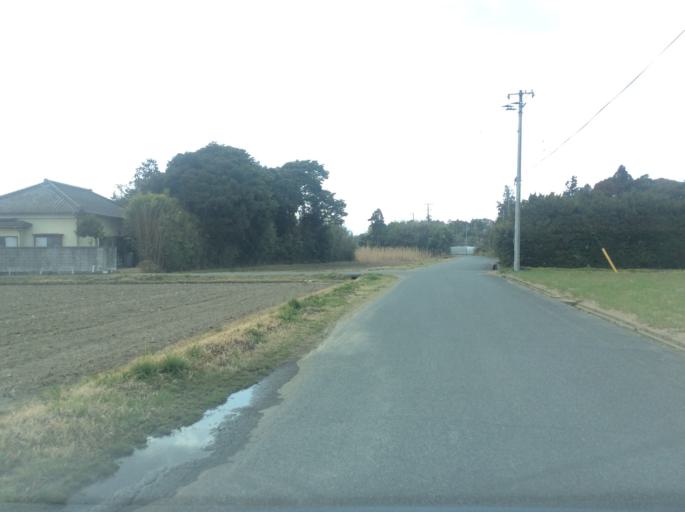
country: JP
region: Fukushima
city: Iwaki
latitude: 37.0770
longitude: 140.9720
